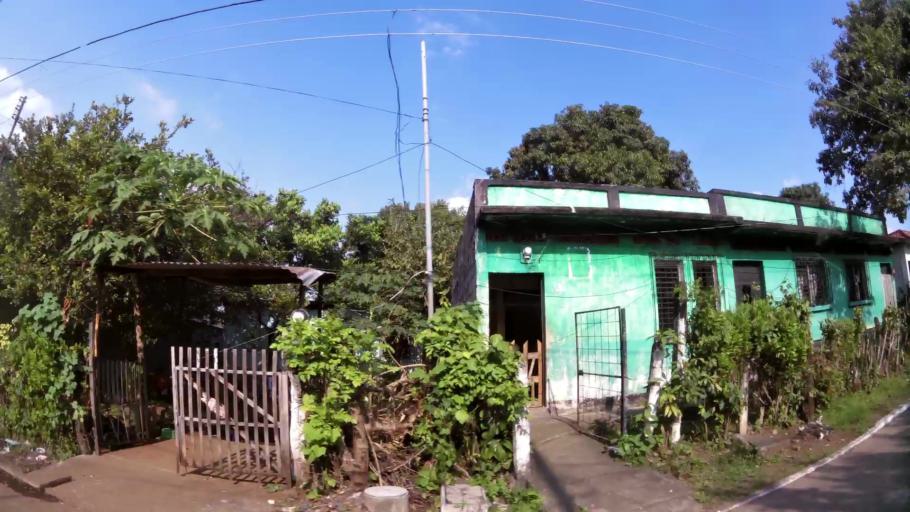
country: GT
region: Retalhuleu
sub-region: Municipio de Retalhuleu
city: Retalhuleu
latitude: 14.5288
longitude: -91.6898
